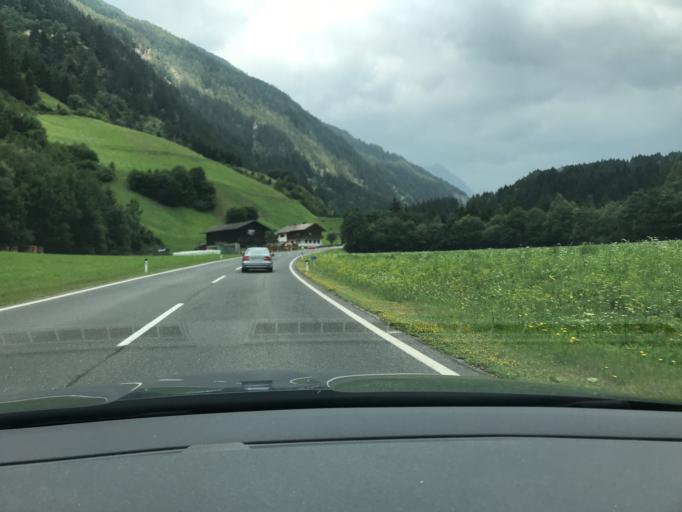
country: AT
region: Tyrol
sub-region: Politischer Bezirk Lienz
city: Hopfgarten in Defereggen
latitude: 46.9552
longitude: 12.5593
